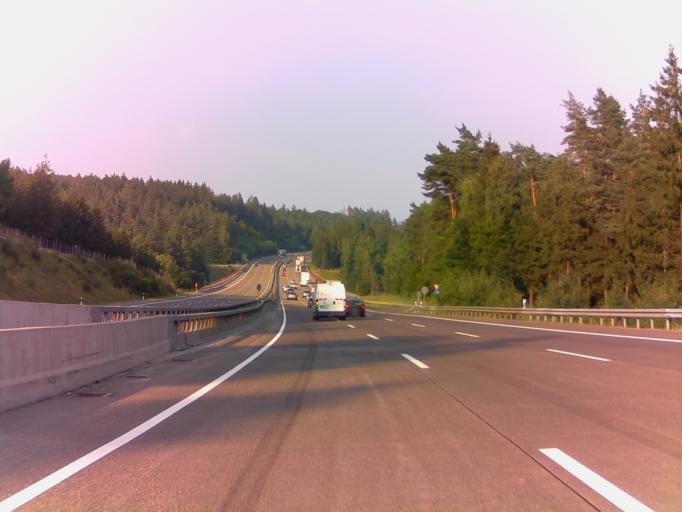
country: DE
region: Hesse
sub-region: Regierungsbezirk Kassel
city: Niederaula
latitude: 50.8421
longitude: 9.6216
